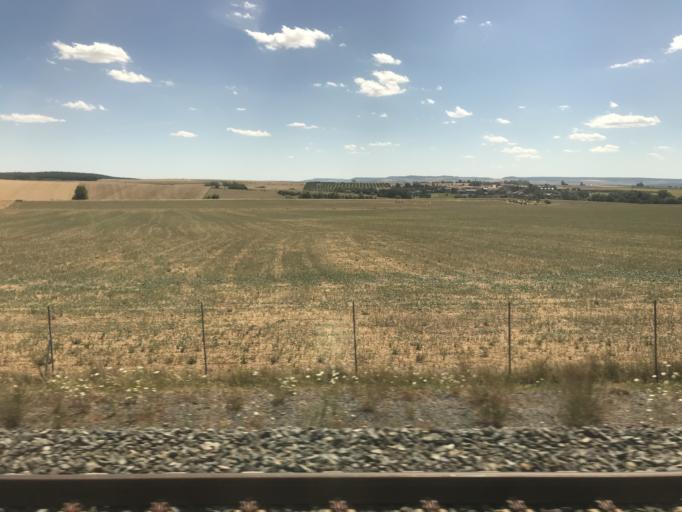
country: FR
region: Lorraine
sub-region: Departement de la Moselle
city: Verny
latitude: 48.9570
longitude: 6.2199
